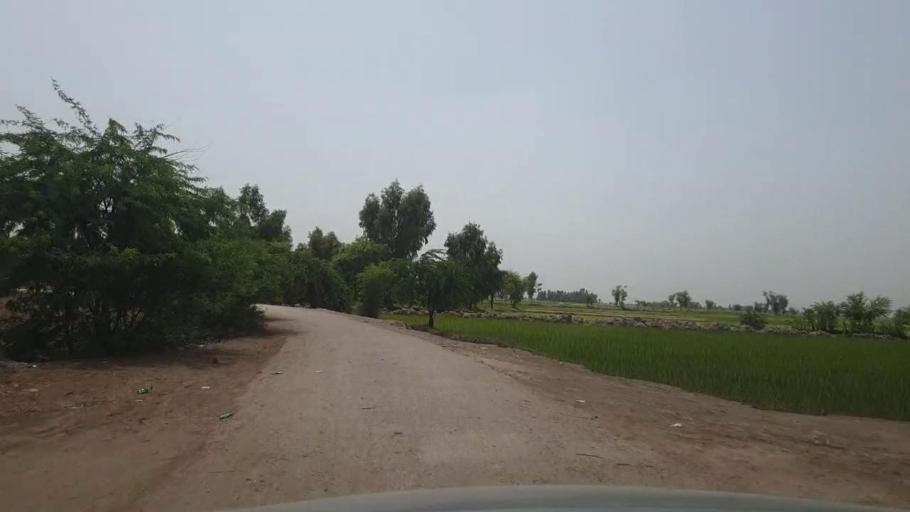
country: PK
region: Sindh
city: Garhi Yasin
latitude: 27.9268
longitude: 68.4019
